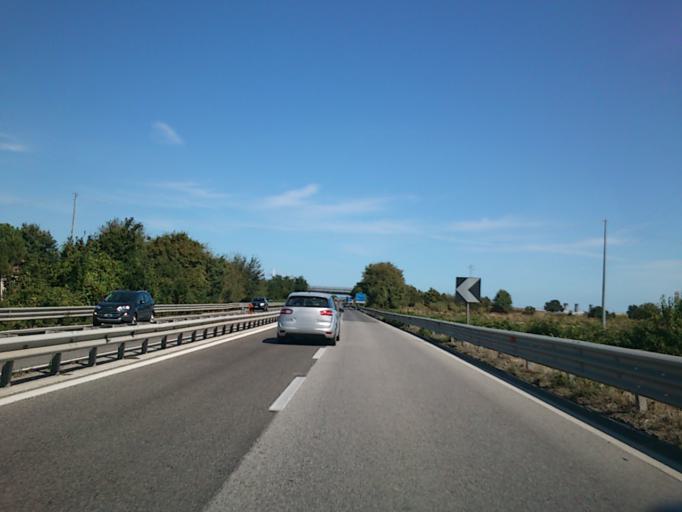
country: IT
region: The Marches
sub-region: Provincia di Pesaro e Urbino
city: Bellocchi
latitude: 43.7812
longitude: 12.9882
